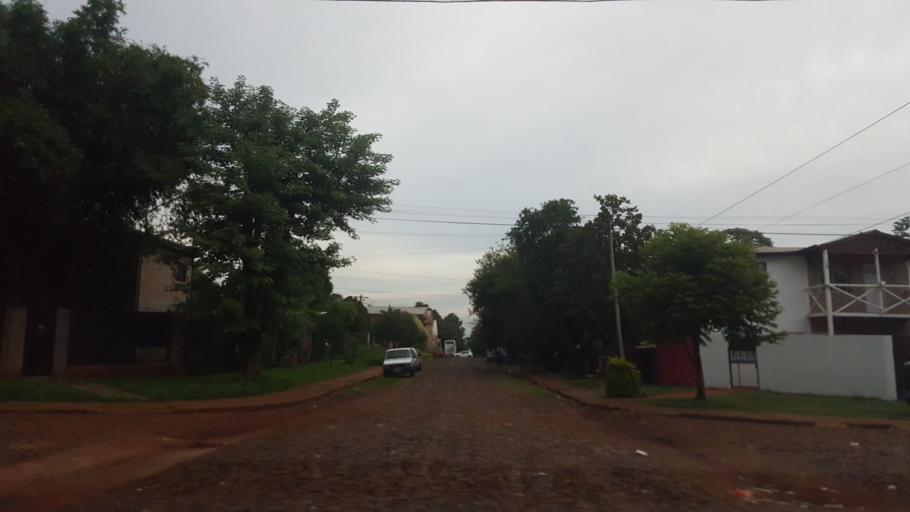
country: AR
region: Misiones
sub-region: Departamento de Capital
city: Posadas
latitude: -27.3949
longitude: -55.9140
